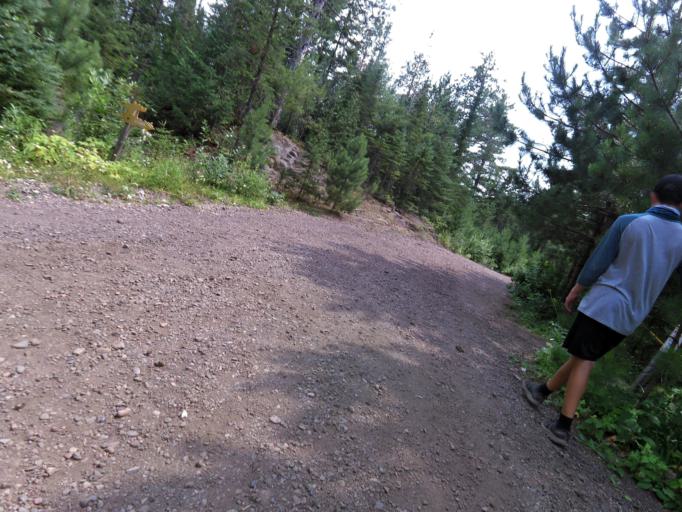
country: CA
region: Ontario
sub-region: Thunder Bay District
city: Thunder Bay
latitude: 48.8013
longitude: -88.6162
